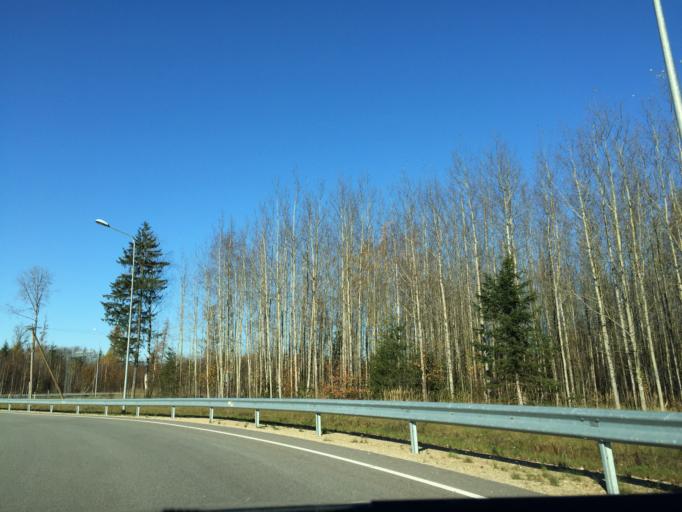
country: LV
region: Skriveri
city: Skriveri
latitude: 56.7317
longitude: 25.1642
